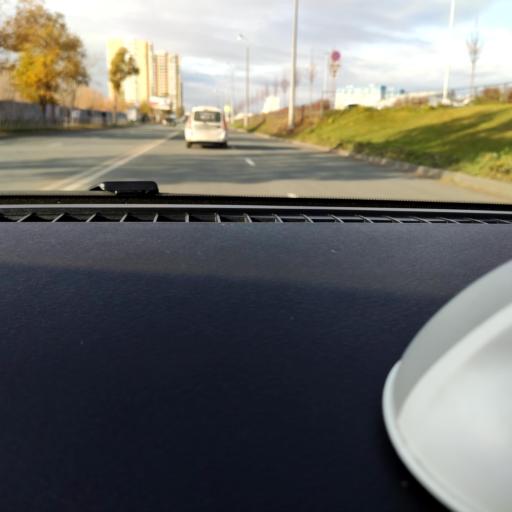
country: RU
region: Samara
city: Samara
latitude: 53.2052
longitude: 50.2005
